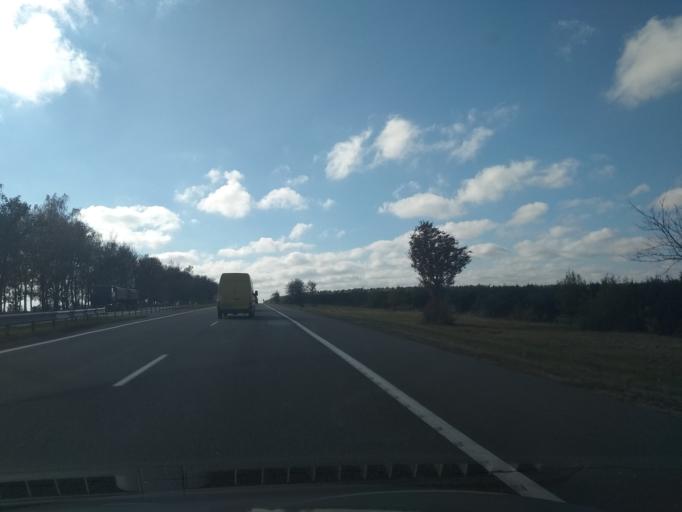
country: BY
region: Minsk
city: Enyerhyetykaw
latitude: 53.6483
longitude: 27.0720
